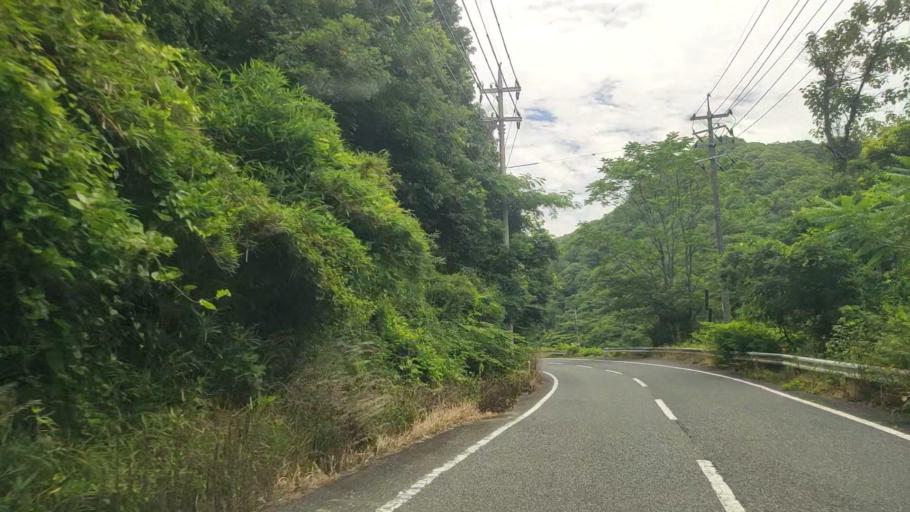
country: JP
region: Okayama
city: Tsuyama
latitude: 35.0665
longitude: 134.2278
